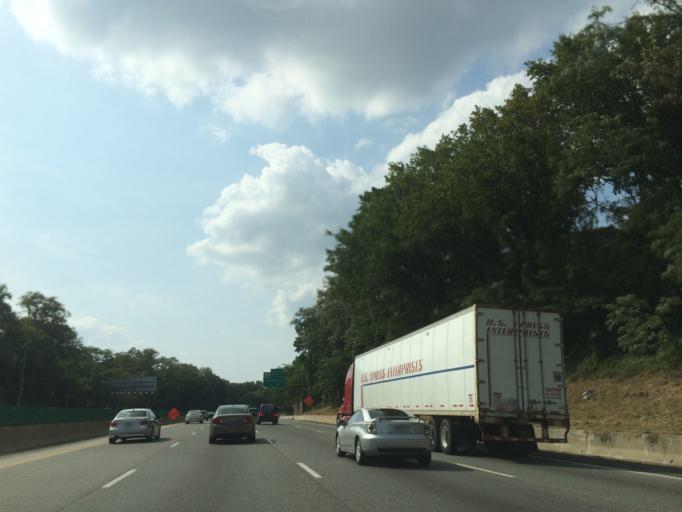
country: US
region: Maryland
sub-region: Baltimore County
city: Catonsville
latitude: 39.2698
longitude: -76.7197
